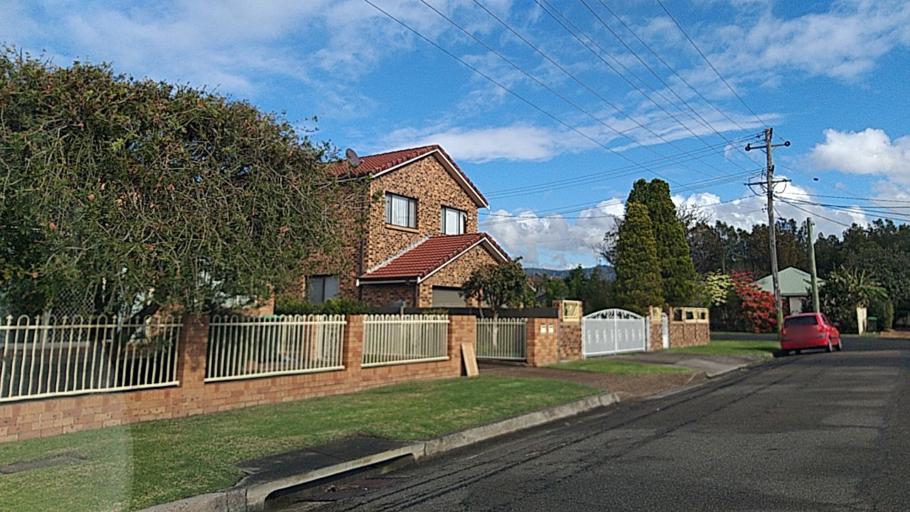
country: AU
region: New South Wales
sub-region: Wollongong
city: East Corrimal
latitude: -34.3736
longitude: 150.9134
